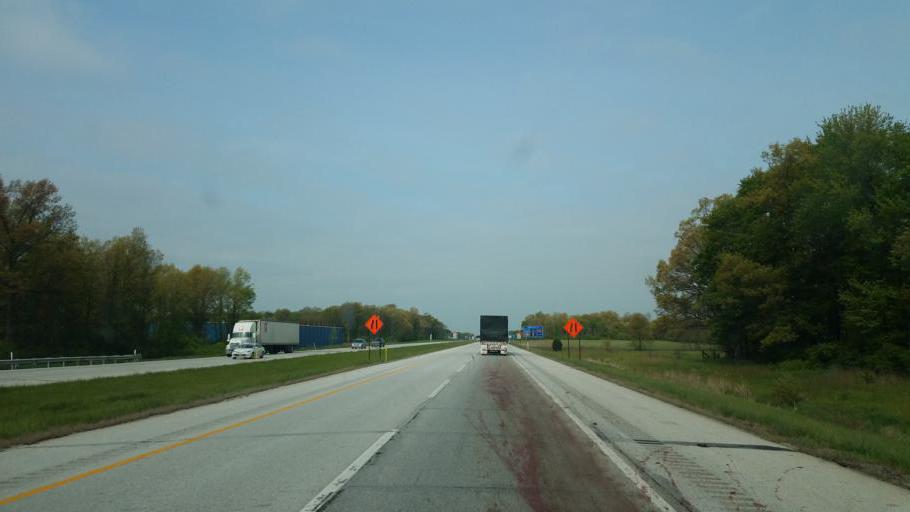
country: US
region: Indiana
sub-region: Elkhart County
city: Simonton Lake
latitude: 41.7300
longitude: -85.9294
